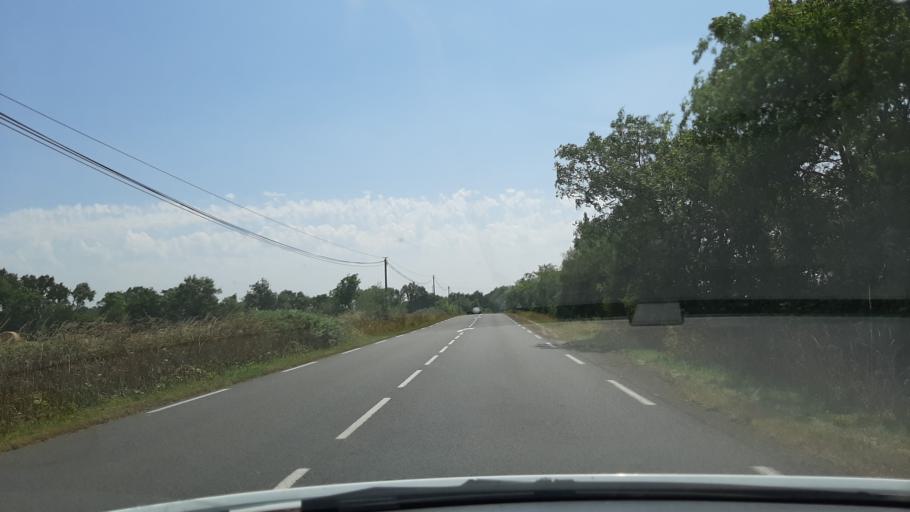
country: FR
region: Pays de la Loire
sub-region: Departement de la Vendee
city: Mouilleron-le-Captif
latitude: 46.7516
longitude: -1.4649
